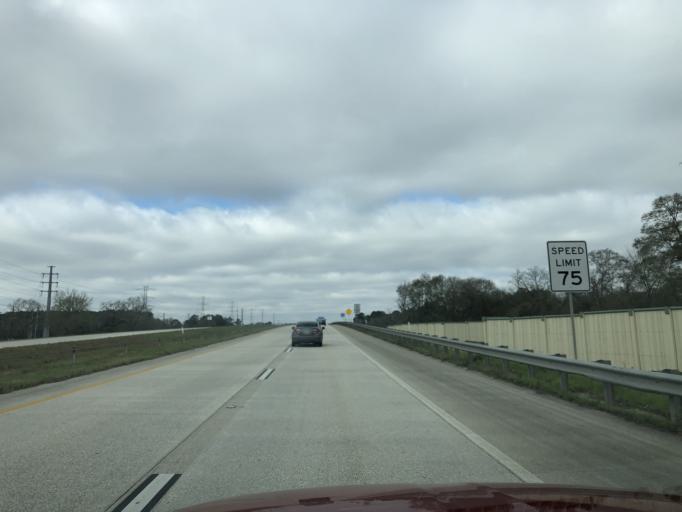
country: US
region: Texas
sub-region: Harris County
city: Spring
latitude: 30.0924
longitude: -95.4751
